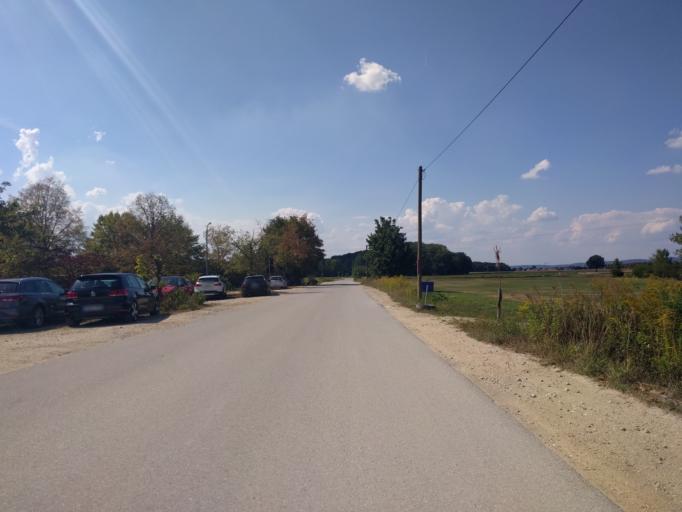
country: DE
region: Bavaria
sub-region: Upper Palatinate
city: Mintraching
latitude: 48.9753
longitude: 12.2714
